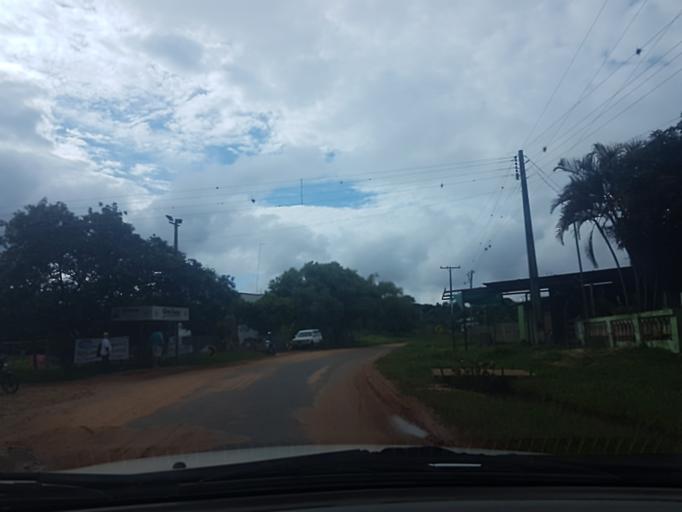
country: PY
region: Central
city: Limpio
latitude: -25.2063
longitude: -57.4488
